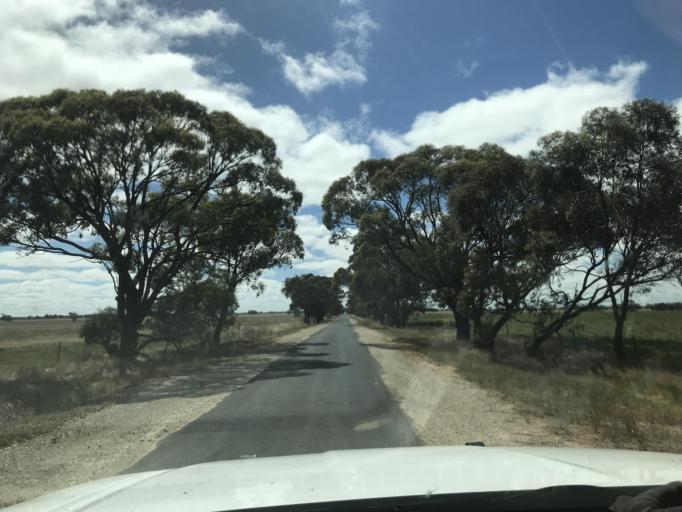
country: AU
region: South Australia
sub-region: Tatiara
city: Bordertown
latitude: -36.2767
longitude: 141.0968
